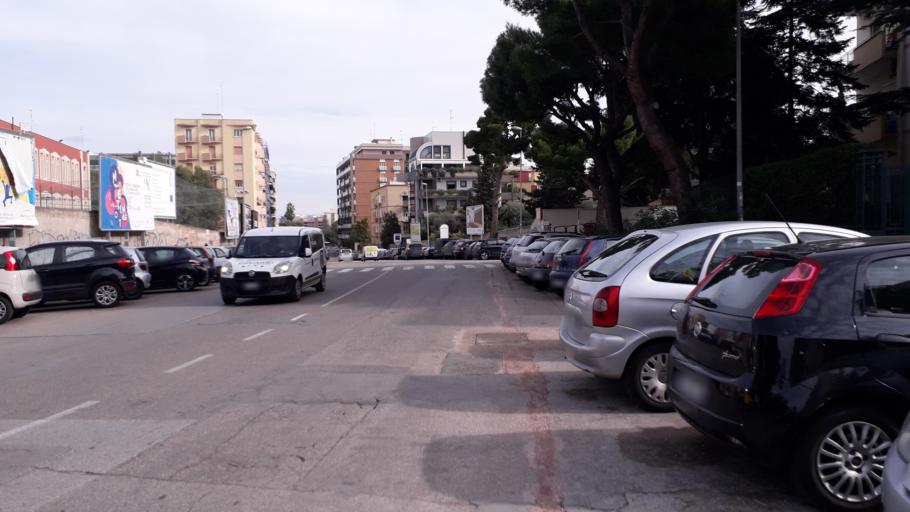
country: IT
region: Apulia
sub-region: Provincia di Bari
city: Bari
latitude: 41.1126
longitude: 16.8777
